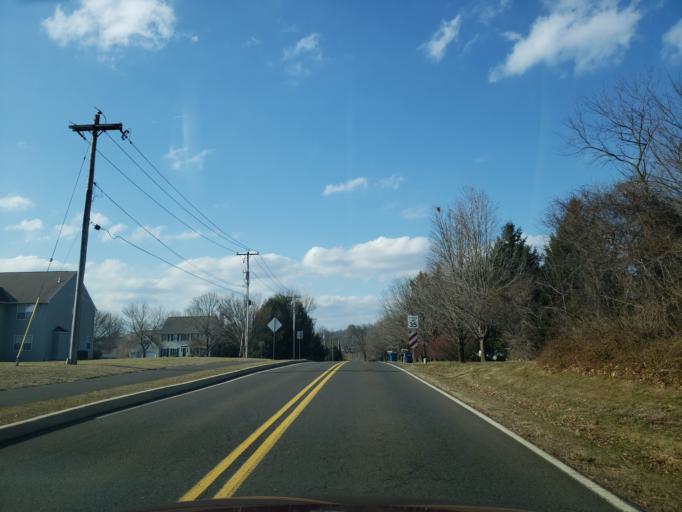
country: US
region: Pennsylvania
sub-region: Bucks County
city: Doylestown
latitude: 40.2917
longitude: -75.1418
